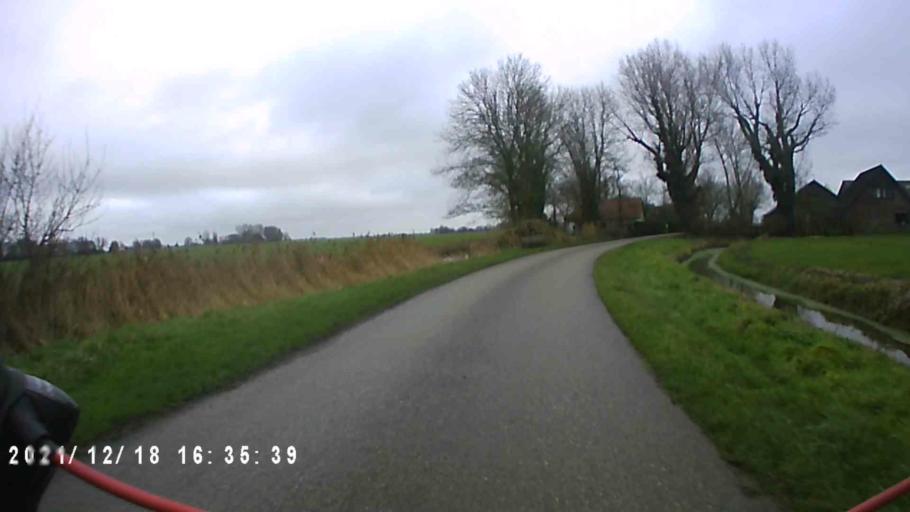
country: NL
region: Friesland
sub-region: Gemeente Dongeradeel
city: Dokkum
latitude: 53.3565
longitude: 6.0207
